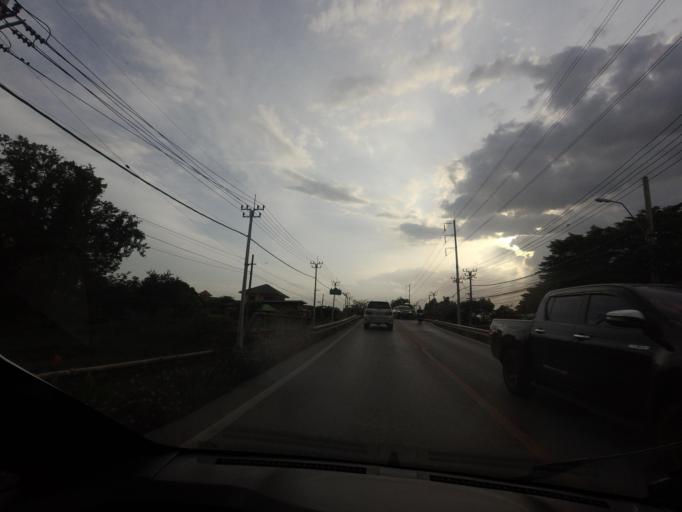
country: TH
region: Bangkok
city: Nong Chok
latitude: 13.8551
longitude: 100.8152
